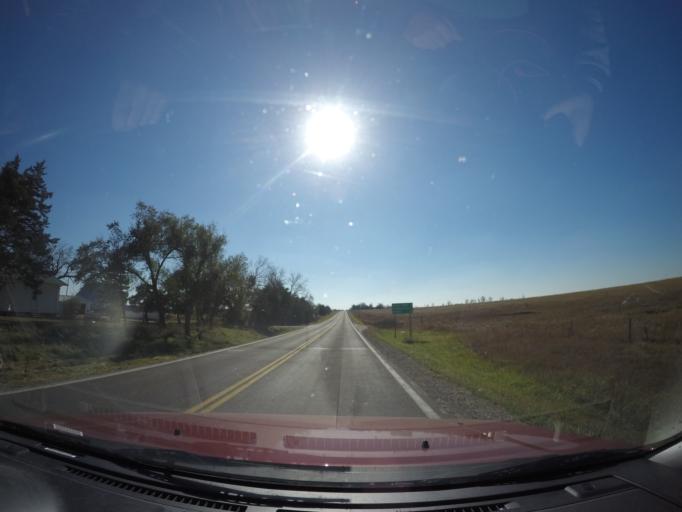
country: US
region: Kansas
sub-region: Morris County
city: Council Grove
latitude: 38.8394
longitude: -96.5015
